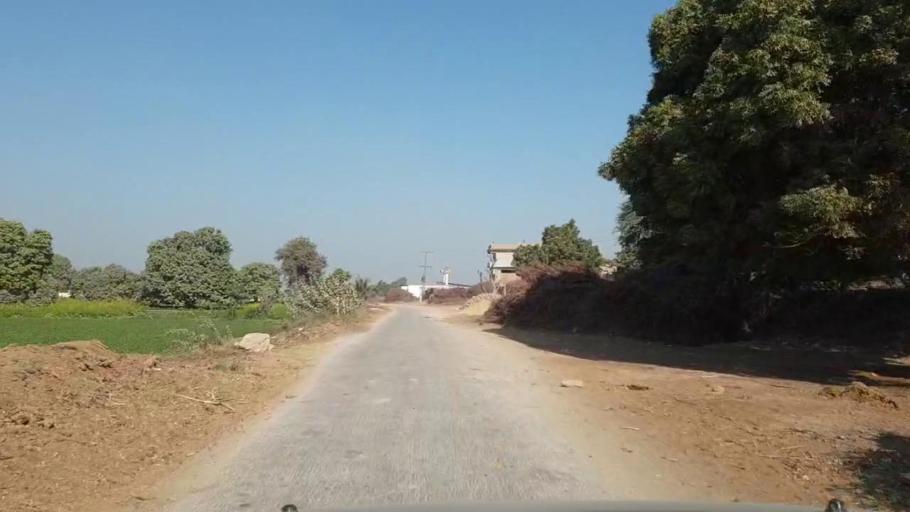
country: PK
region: Sindh
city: Matiari
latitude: 25.5977
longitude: 68.6010
